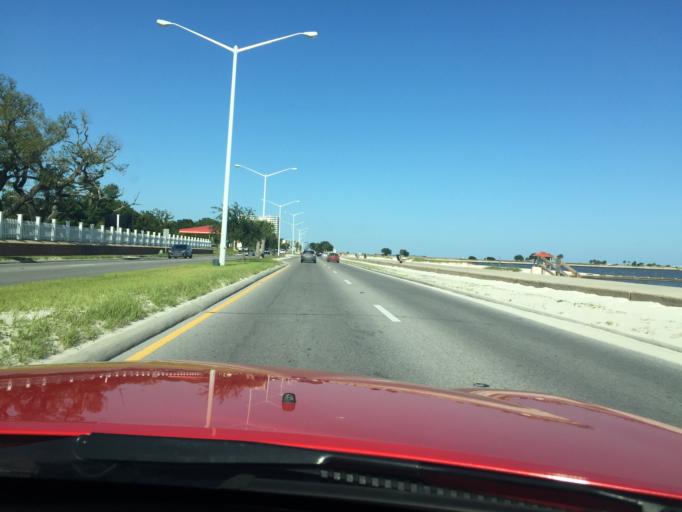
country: US
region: Mississippi
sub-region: Harrison County
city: Biloxi
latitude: 30.3917
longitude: -88.9690
